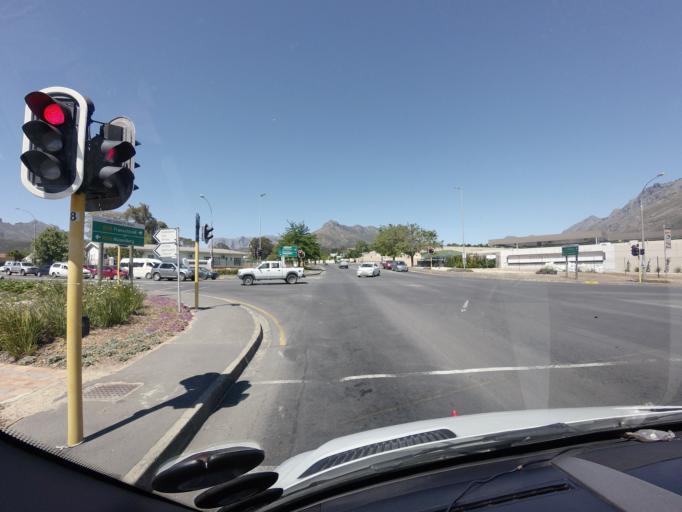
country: ZA
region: Western Cape
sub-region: Cape Winelands District Municipality
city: Stellenbosch
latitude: -33.9252
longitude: 18.8775
